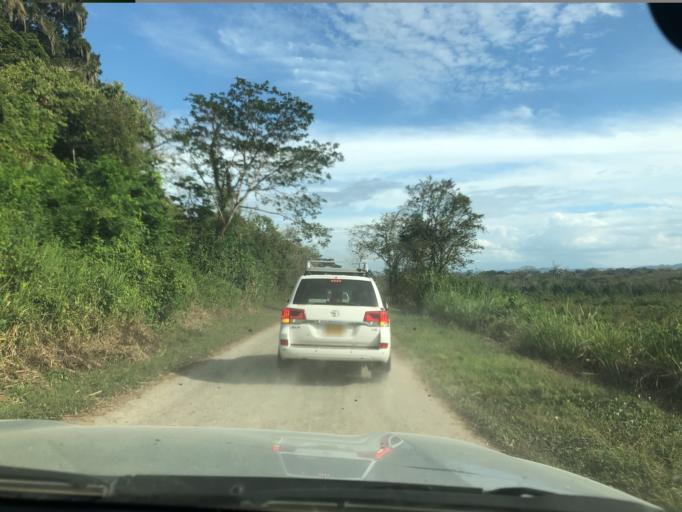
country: CR
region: Alajuela
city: San Jose
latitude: 11.1211
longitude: -85.2870
